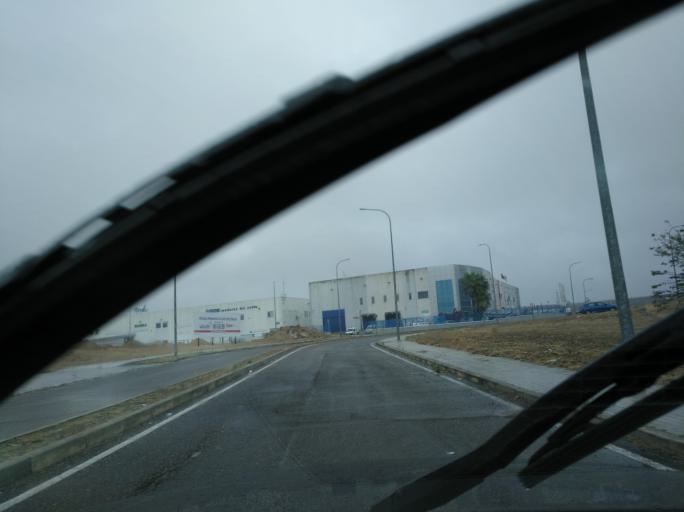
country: ES
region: Extremadura
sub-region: Provincia de Badajoz
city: Badajoz
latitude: 38.8979
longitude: -6.9919
